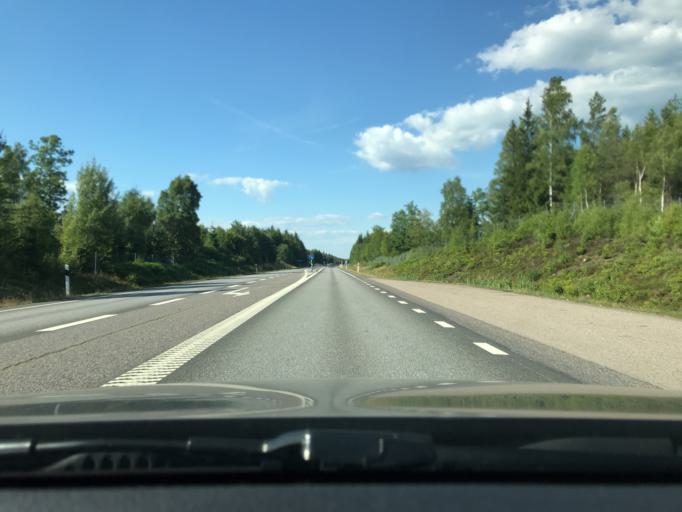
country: SE
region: Kronoberg
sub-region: Almhults Kommun
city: AElmhult
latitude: 56.4734
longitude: 14.1071
